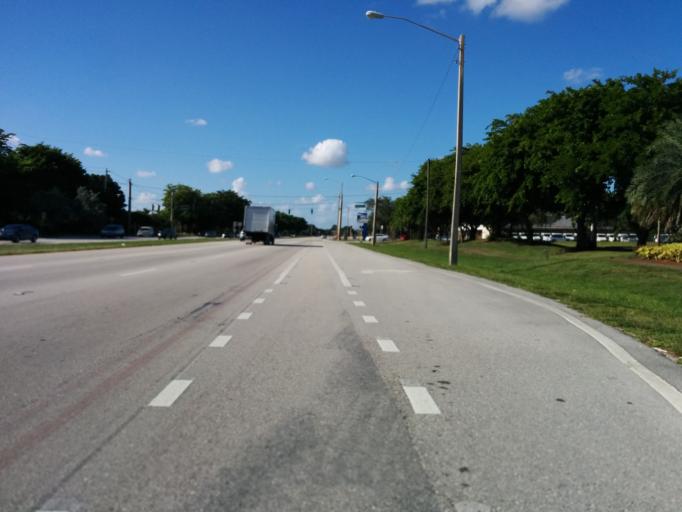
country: US
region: Florida
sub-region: Broward County
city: Davie
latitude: 26.0718
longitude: -80.2523
